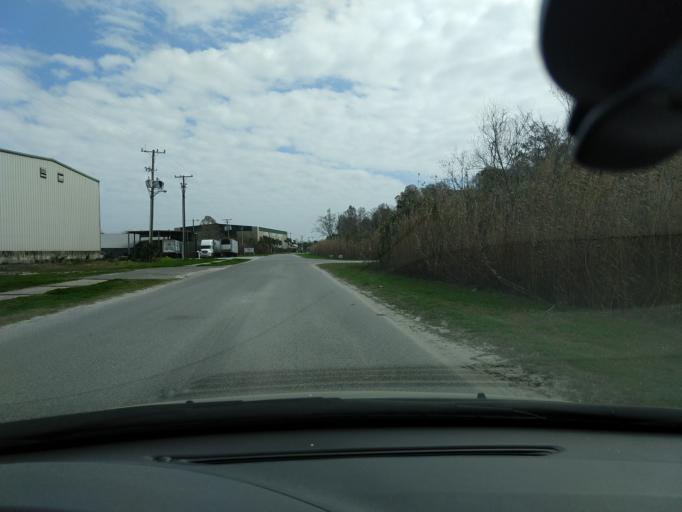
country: US
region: Florida
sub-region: Franklin County
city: Apalachicola
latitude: 29.7330
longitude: -84.9934
